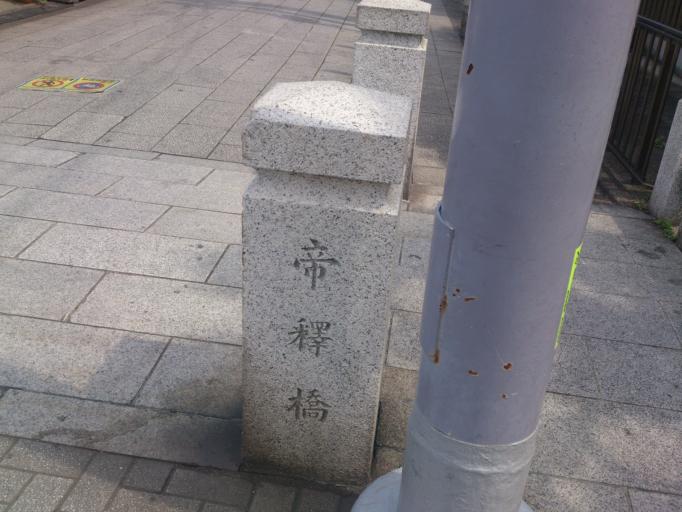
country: JP
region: Chiba
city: Matsudo
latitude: 35.7571
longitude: 139.8759
